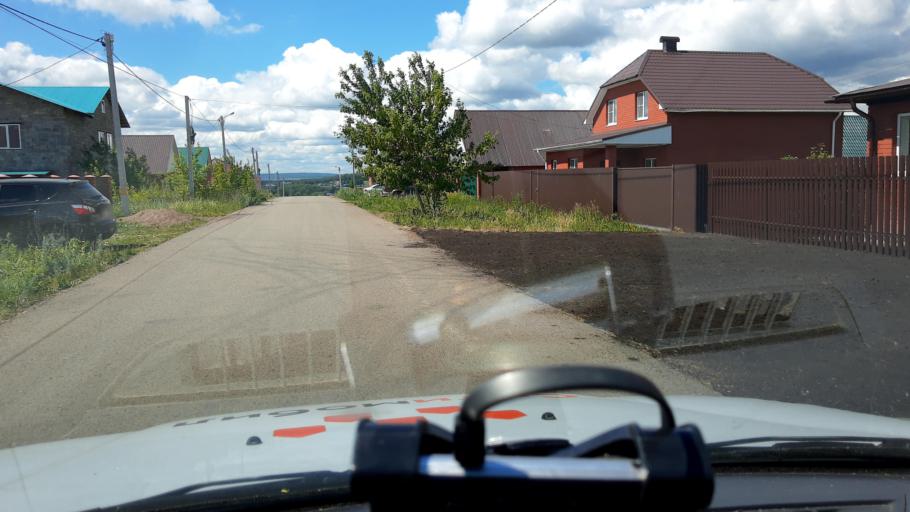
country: RU
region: Bashkortostan
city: Avdon
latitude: 54.6459
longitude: 55.7322
